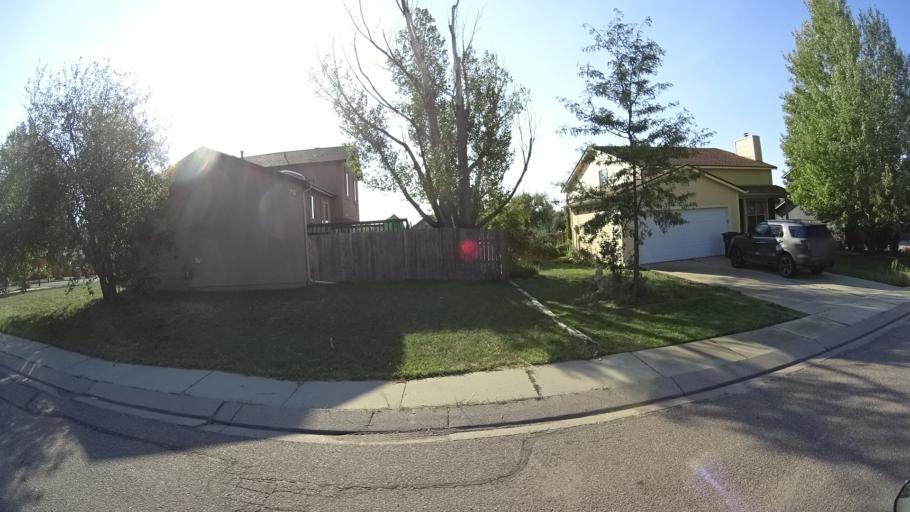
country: US
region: Colorado
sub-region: El Paso County
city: Stratmoor
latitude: 38.7748
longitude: -104.8015
